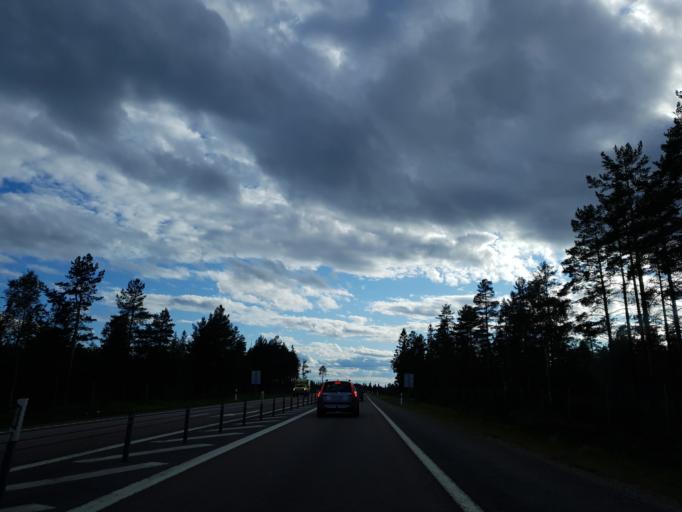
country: SE
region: Vaesternorrland
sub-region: Haernoesands Kommun
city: Haernoesand
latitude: 62.5672
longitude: 17.7354
